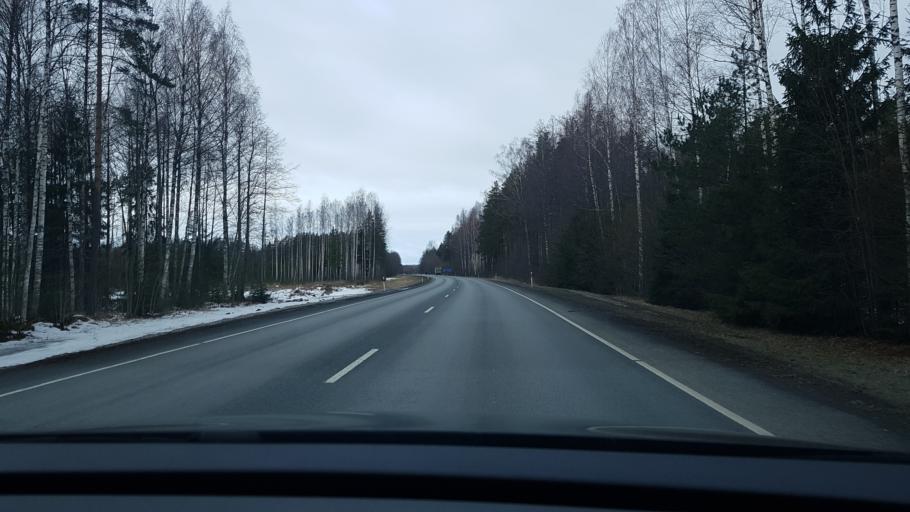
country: EE
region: Paernumaa
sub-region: Paikuse vald
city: Paikuse
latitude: 58.2555
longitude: 24.6798
